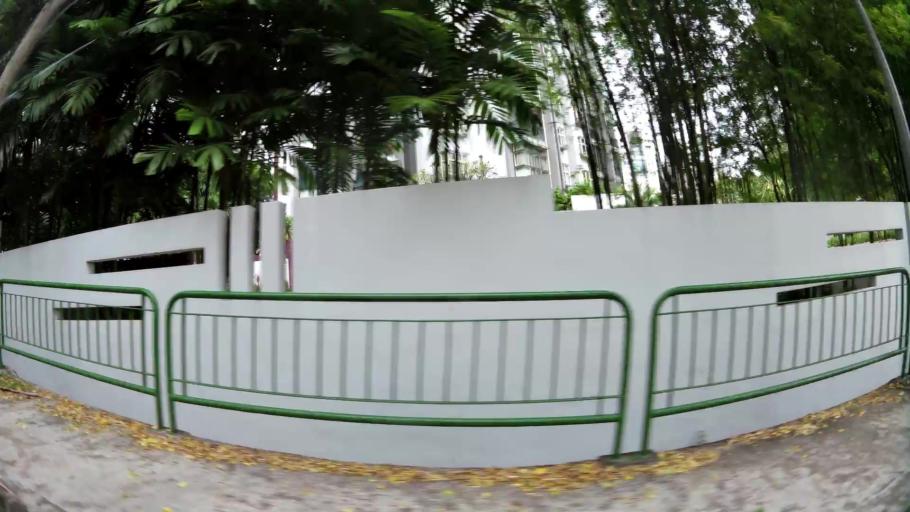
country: SG
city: Singapore
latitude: 1.3241
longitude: 103.8495
